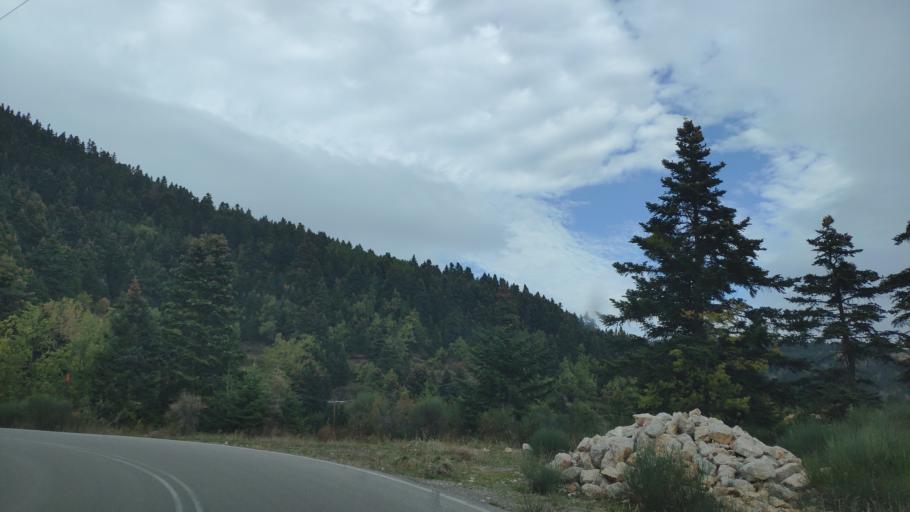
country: GR
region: Central Greece
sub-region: Nomos Fokidos
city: Amfissa
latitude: 38.6900
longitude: 22.3204
